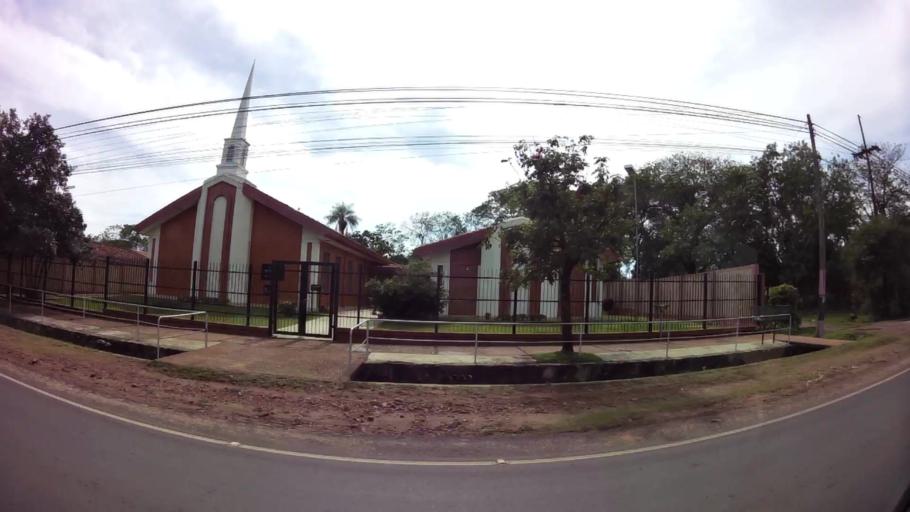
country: PY
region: Presidente Hayes
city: Villa Hayes
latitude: -25.1075
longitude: -57.4906
